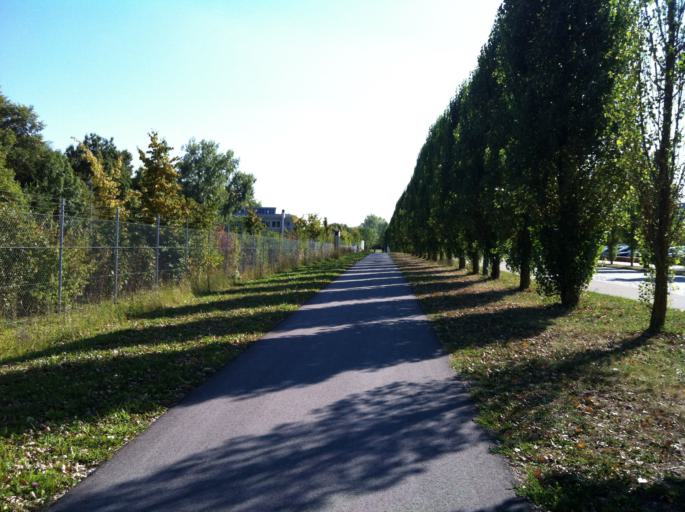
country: DE
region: Bavaria
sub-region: Upper Bavaria
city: Garching bei Munchen
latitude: 48.2636
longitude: 11.6710
